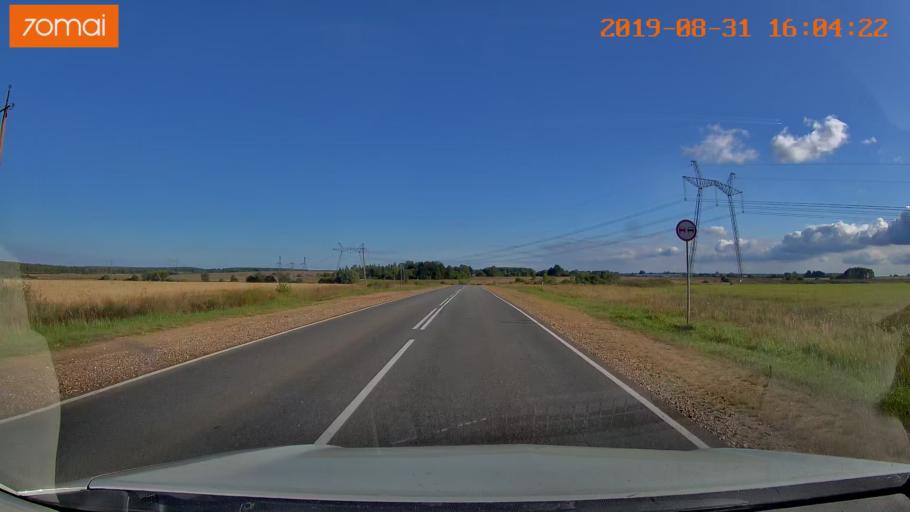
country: RU
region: Kaluga
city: Yukhnov
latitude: 54.6552
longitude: 35.3282
